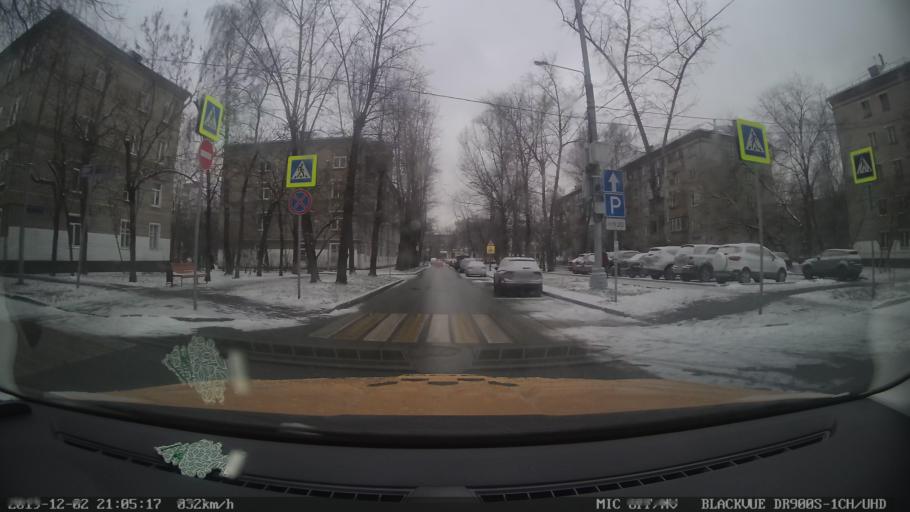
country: RU
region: Moscow
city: Mar'ina Roshcha
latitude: 55.7957
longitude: 37.6222
